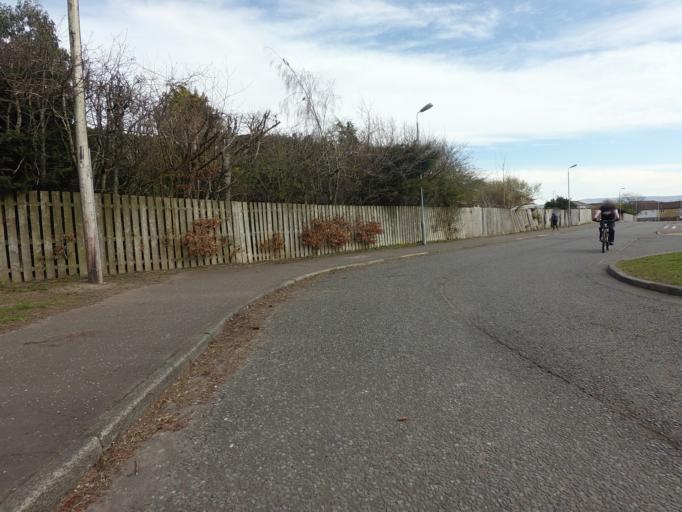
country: GB
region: Scotland
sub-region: West Lothian
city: Livingston
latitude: 55.9072
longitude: -3.5483
